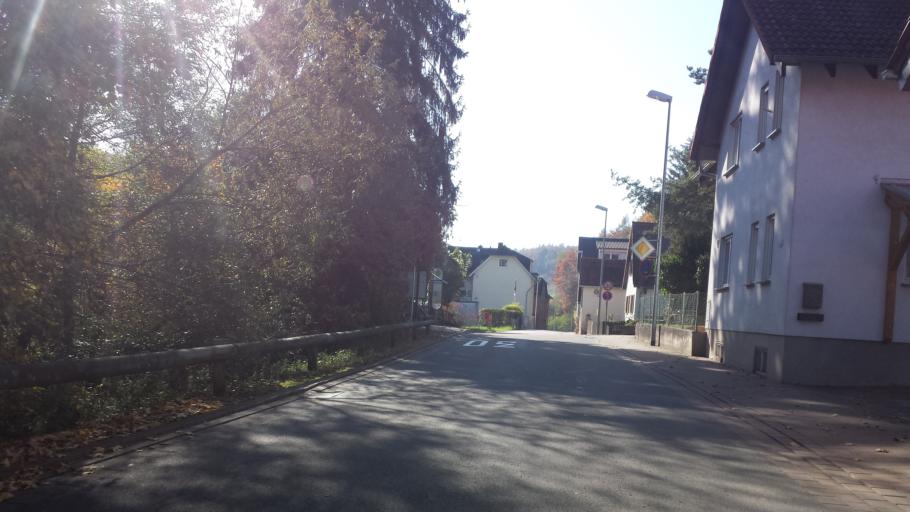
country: DE
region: Hesse
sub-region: Regierungsbezirk Darmstadt
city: Bensheim
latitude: 49.7100
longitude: 8.6483
